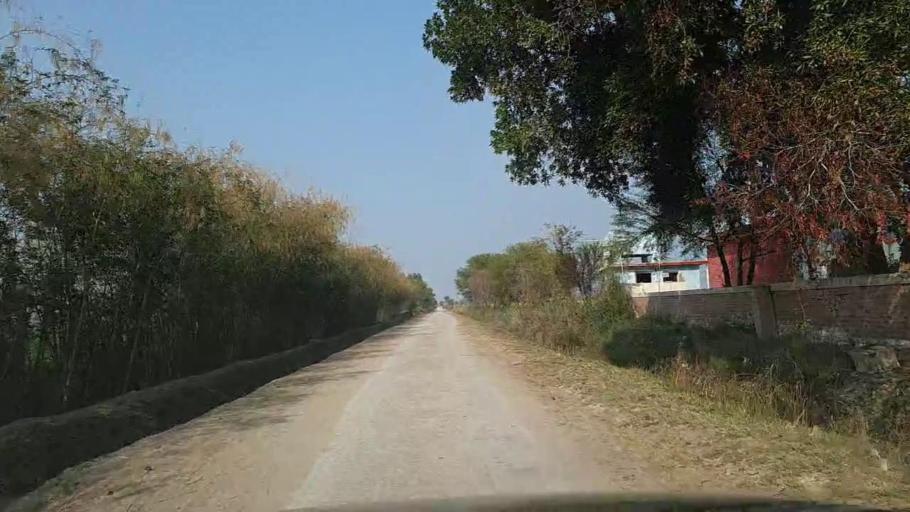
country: PK
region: Sindh
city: Daur
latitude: 26.3983
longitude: 68.4238
